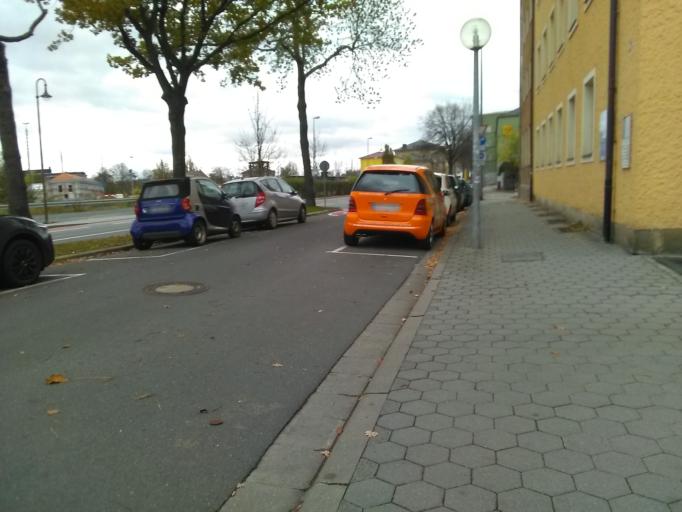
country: DE
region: Bavaria
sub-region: Upper Franconia
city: Bayreuth
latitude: 49.9518
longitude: 11.5787
